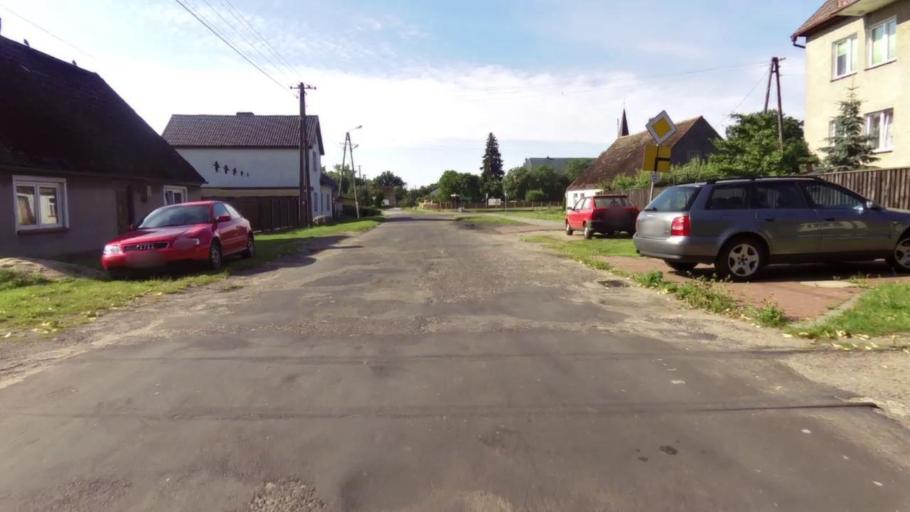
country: PL
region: West Pomeranian Voivodeship
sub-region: Powiat stargardzki
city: Marianowo
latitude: 53.3812
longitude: 15.2670
